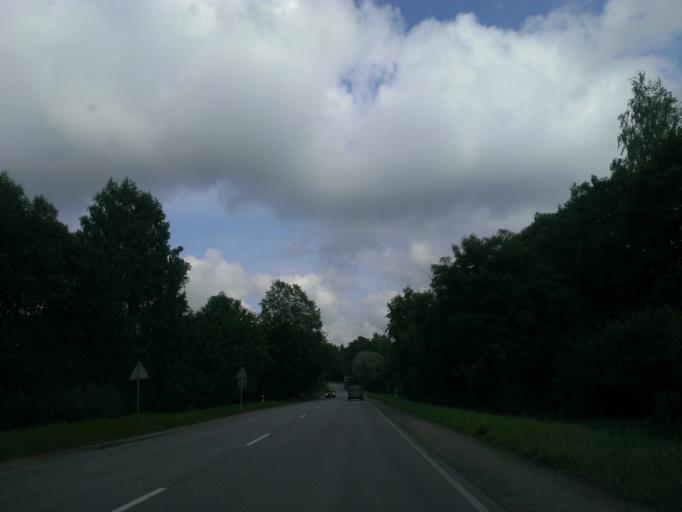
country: LV
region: Priekuli
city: Priekuli
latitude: 57.2554
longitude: 25.3720
